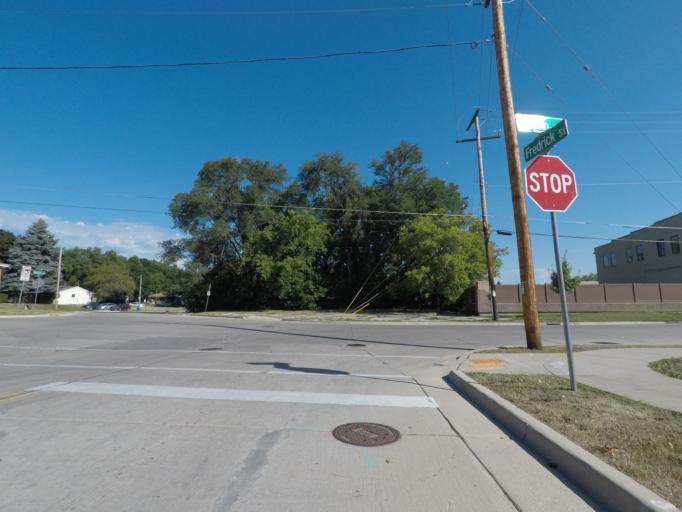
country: US
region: Wisconsin
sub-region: Waukesha County
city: Waukesha
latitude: 43.0091
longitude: -88.2125
